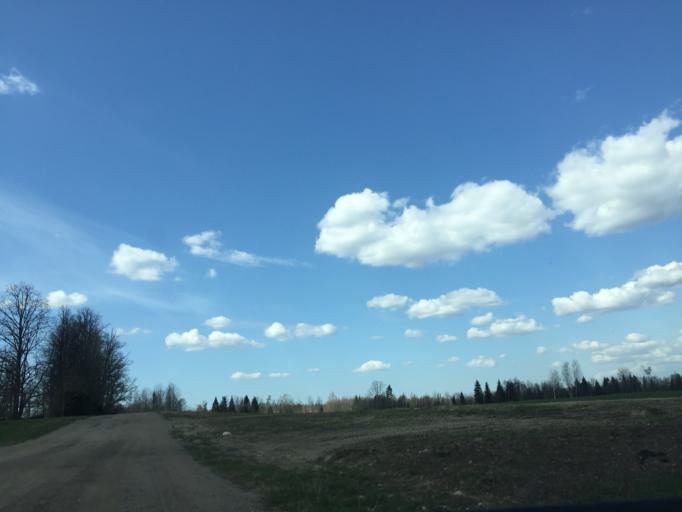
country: LV
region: Skriveri
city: Skriveri
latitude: 56.7933
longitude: 25.1532
